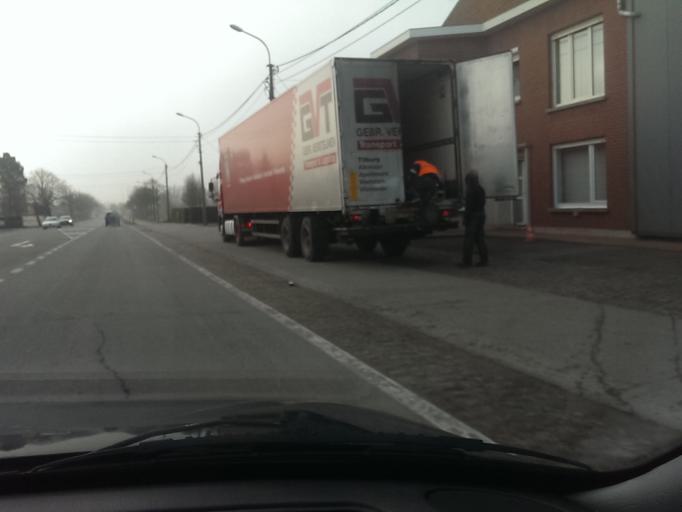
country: BE
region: Flanders
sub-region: Provincie West-Vlaanderen
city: Ledegem
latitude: 50.8629
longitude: 3.1100
